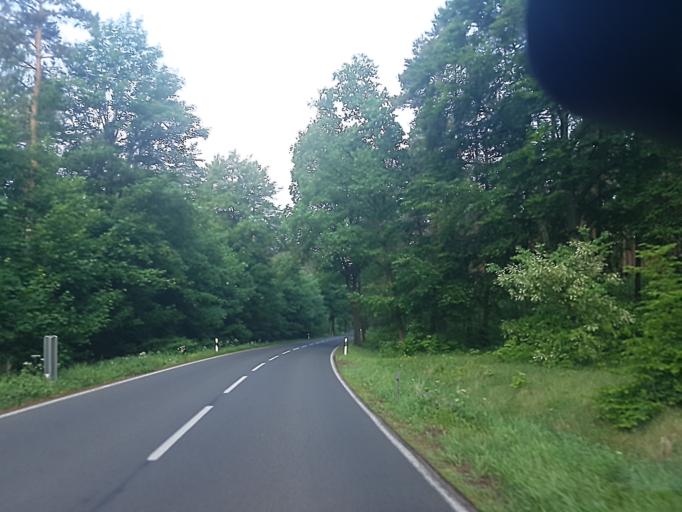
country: DE
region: Saxony-Anhalt
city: Rosslau
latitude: 51.9893
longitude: 12.2922
